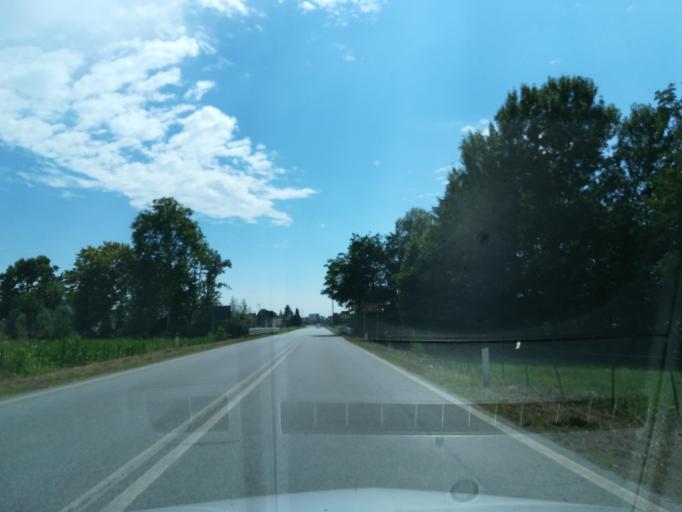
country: IT
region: Lombardy
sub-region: Provincia di Bergamo
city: Almenno San Bartolomeo
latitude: 45.7331
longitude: 9.5772
